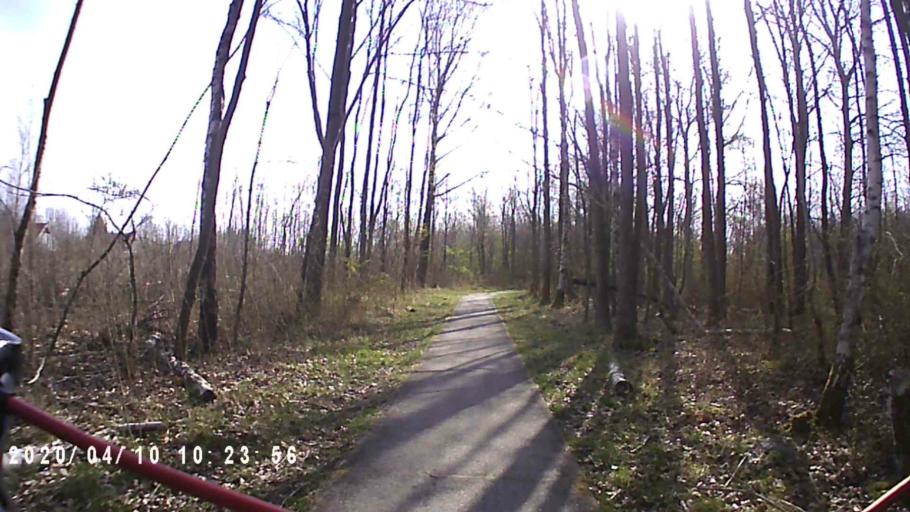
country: NL
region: Friesland
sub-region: Gemeente Dongeradeel
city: Anjum
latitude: 53.3850
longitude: 6.2179
